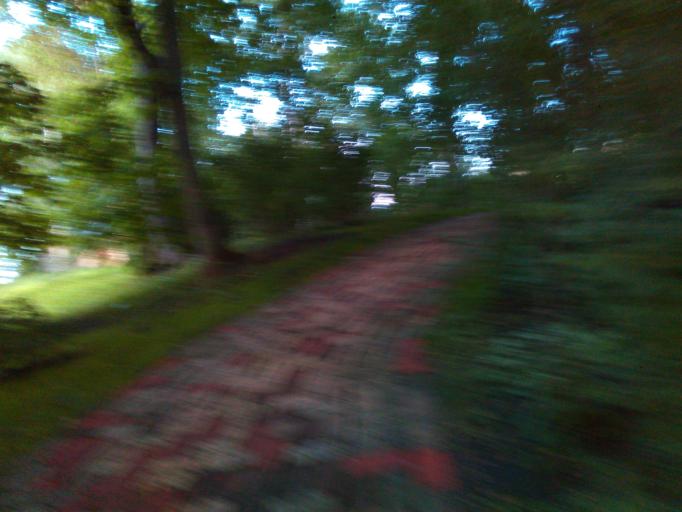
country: RU
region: Penza
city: Lermontovo
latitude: 52.9927
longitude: 43.6716
